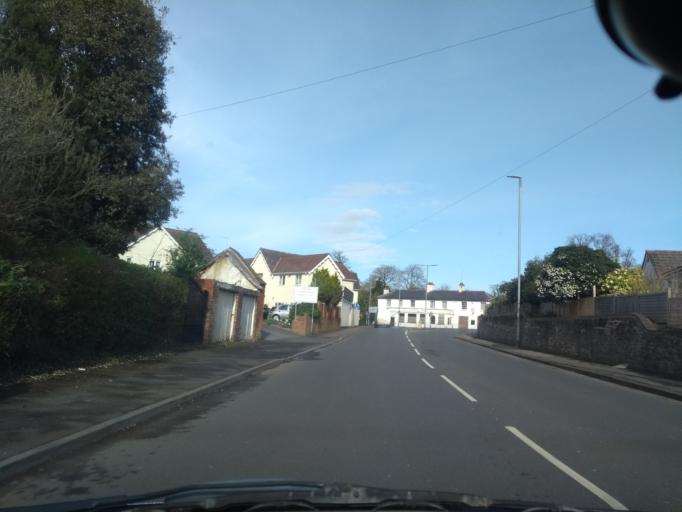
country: GB
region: England
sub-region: Somerset
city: Taunton
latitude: 51.0278
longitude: -3.1201
